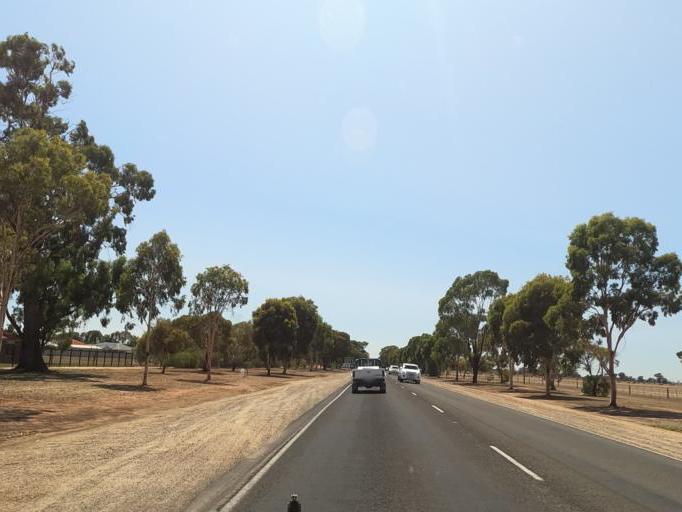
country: AU
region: Victoria
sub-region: Moira
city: Yarrawonga
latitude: -36.0145
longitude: 146.0149
